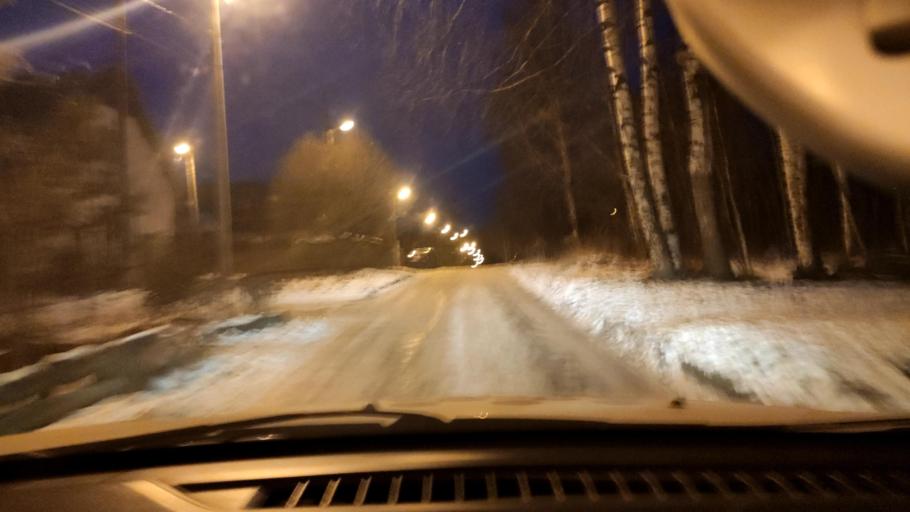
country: RU
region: Perm
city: Kondratovo
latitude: 58.0471
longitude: 56.1098
